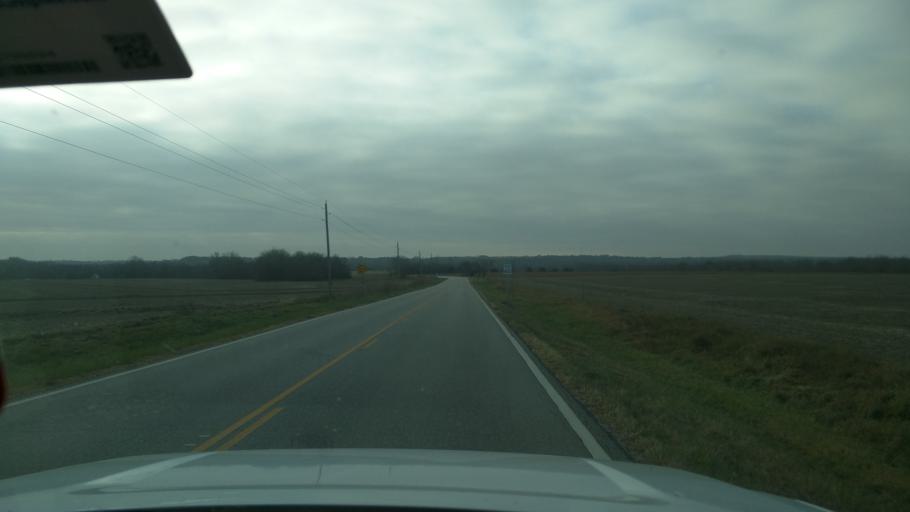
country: US
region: Kansas
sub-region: Greenwood County
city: Eureka
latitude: 37.7210
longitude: -96.2298
